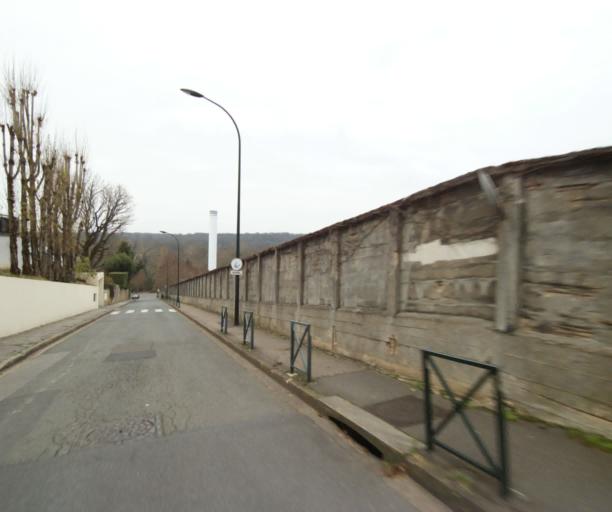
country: FR
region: Ile-de-France
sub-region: Departement des Hauts-de-Seine
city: Garches
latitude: 48.8403
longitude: 2.1717
